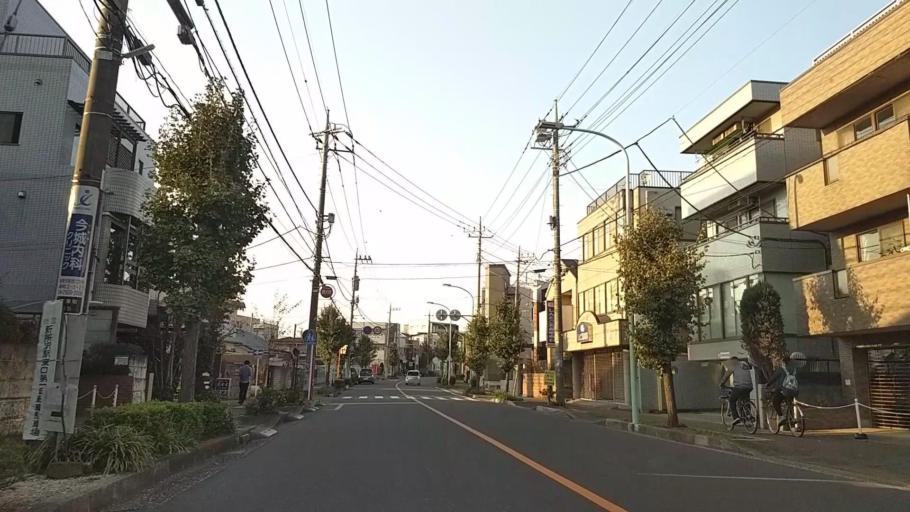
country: JP
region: Saitama
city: Tokorozawa
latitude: 35.8088
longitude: 139.4574
